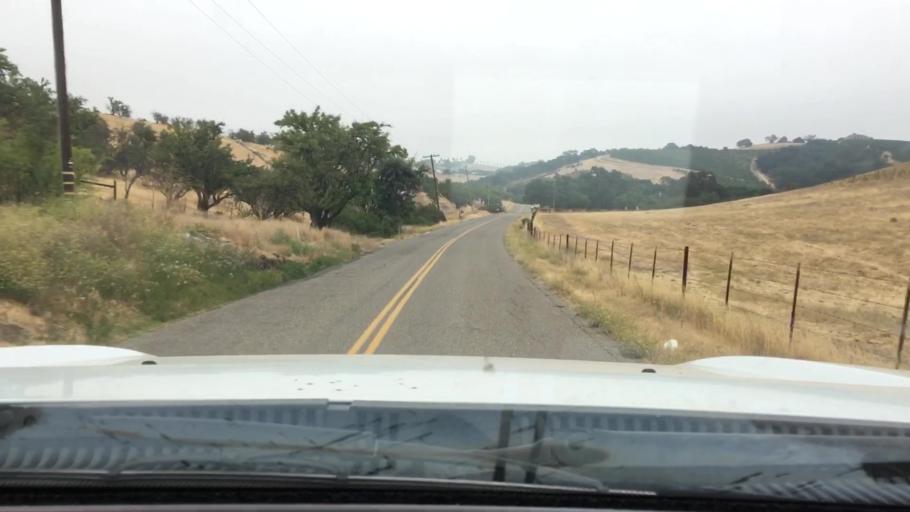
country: US
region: California
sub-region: San Luis Obispo County
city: Atascadero
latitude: 35.5305
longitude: -120.6263
